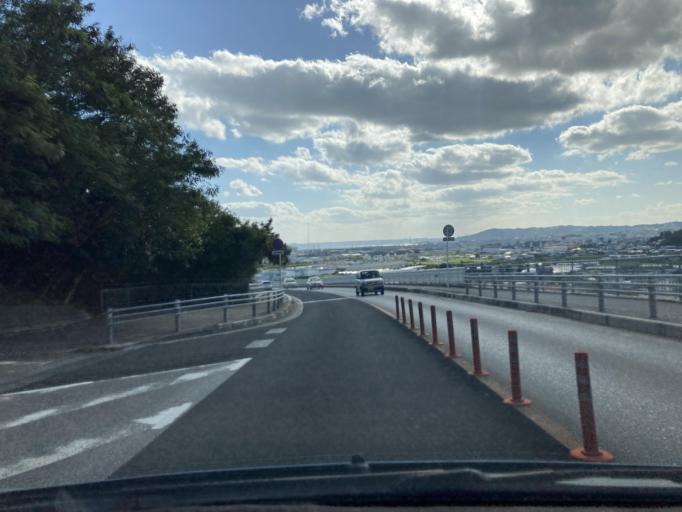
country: JP
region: Okinawa
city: Gushikawa
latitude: 26.3506
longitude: 127.8563
